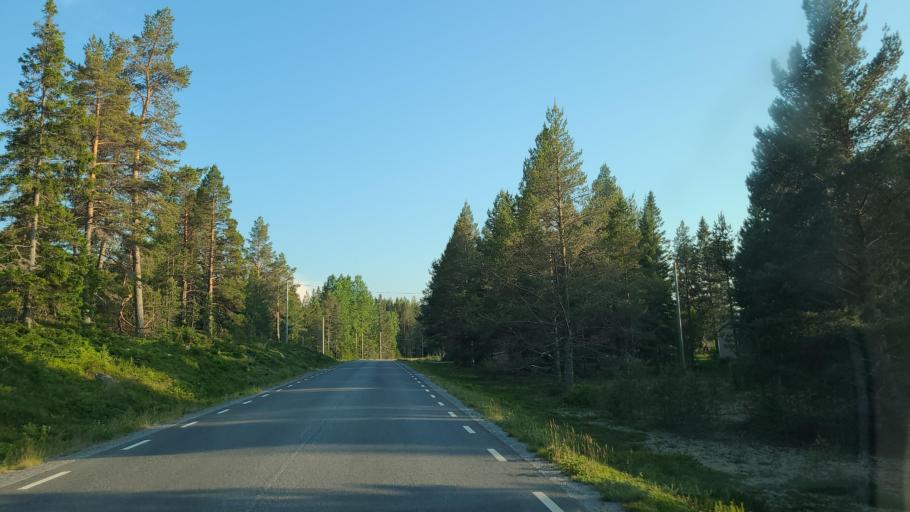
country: SE
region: Vaesterbotten
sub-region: Skelleftea Kommun
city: Burea
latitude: 64.4562
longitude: 21.5802
